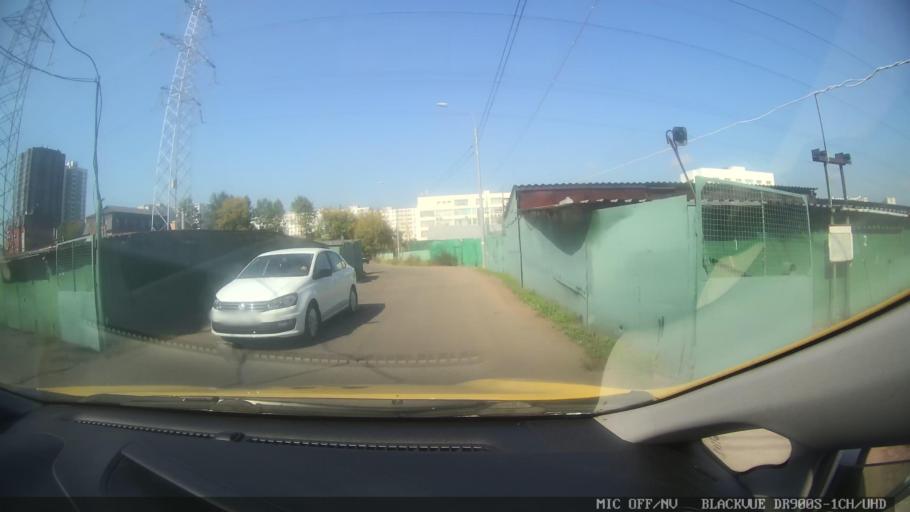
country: RU
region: Moscow
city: Bibirevo
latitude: 55.8801
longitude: 37.6016
